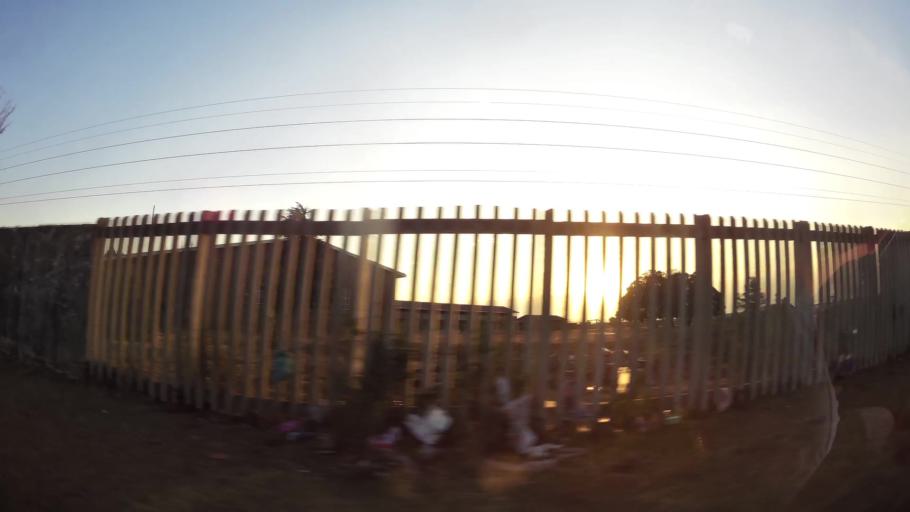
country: ZA
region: Gauteng
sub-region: West Rand District Municipality
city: Randfontein
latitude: -26.1999
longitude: 27.7082
